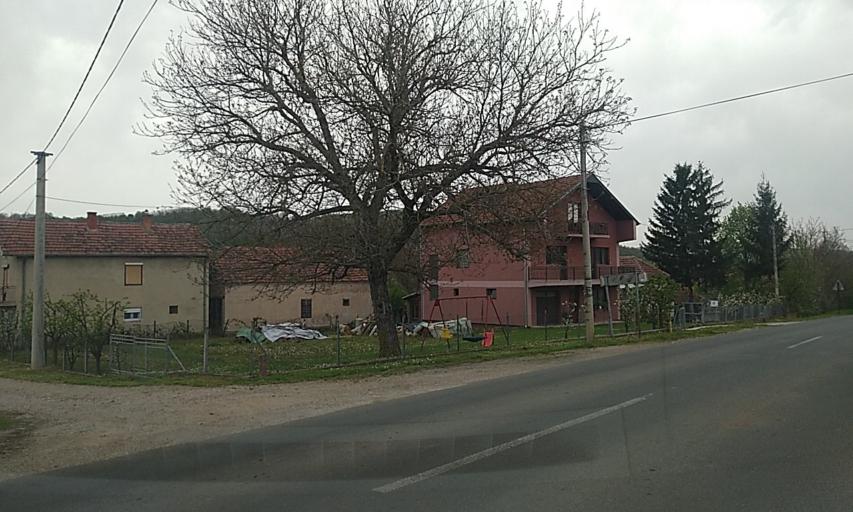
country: RS
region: Central Serbia
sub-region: Nisavski Okrug
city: Razanj
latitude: 43.5736
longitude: 21.5024
